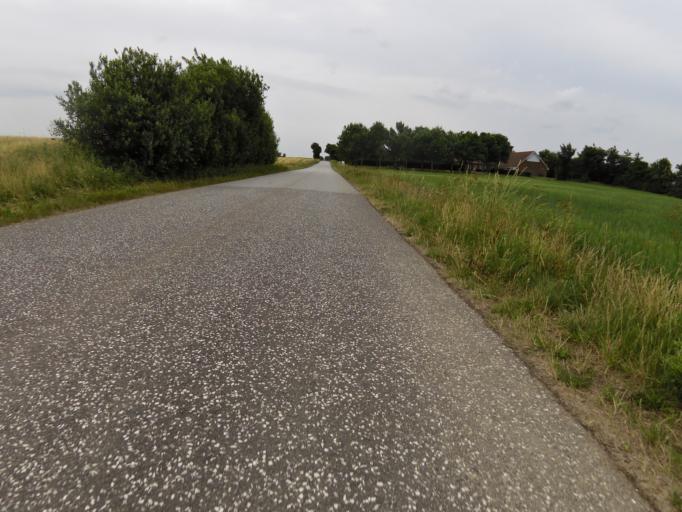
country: DK
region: Central Jutland
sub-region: Holstebro Kommune
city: Holstebro
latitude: 56.4137
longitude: 8.6712
